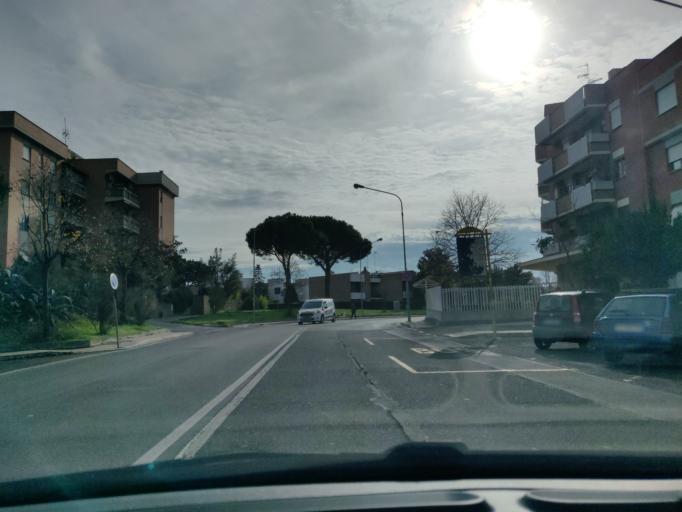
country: IT
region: Latium
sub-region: Citta metropolitana di Roma Capitale
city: Civitavecchia
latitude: 42.1021
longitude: 11.8090
